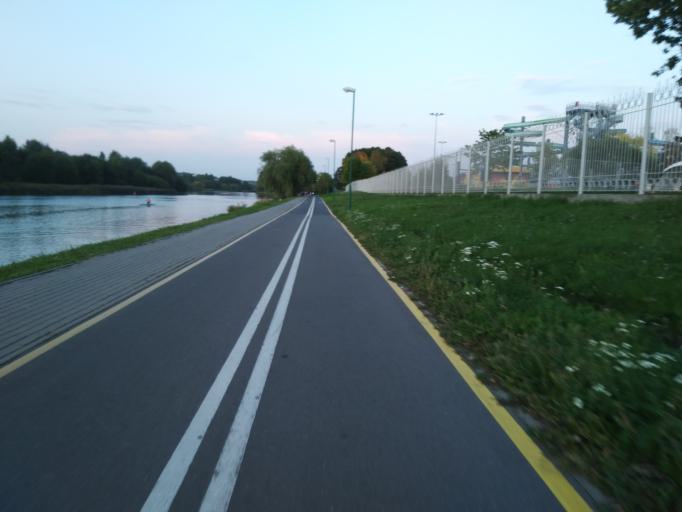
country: BY
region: Minsk
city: Minsk
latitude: 53.9323
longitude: 27.5160
